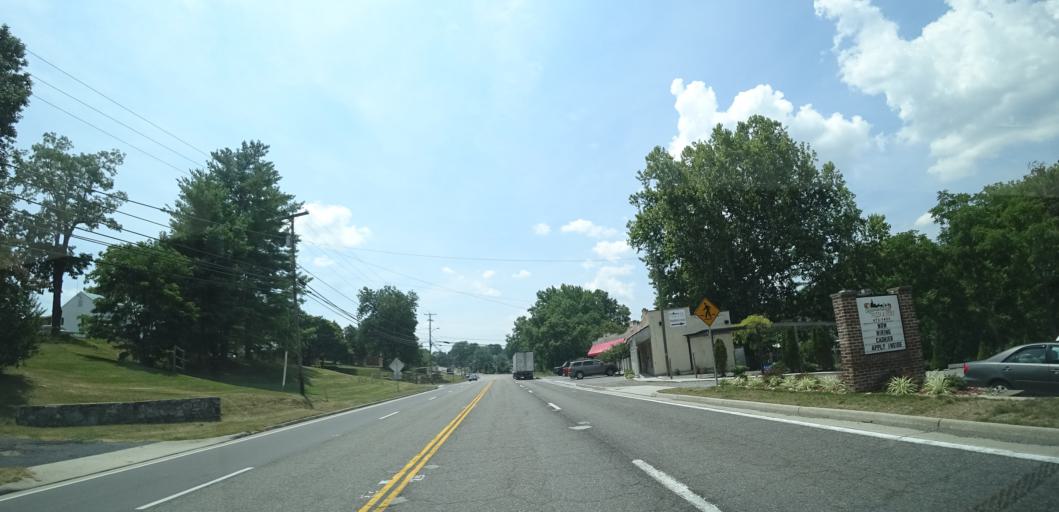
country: US
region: Virginia
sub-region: Botetourt County
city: Fincastle
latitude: 37.4998
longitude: -79.8794
